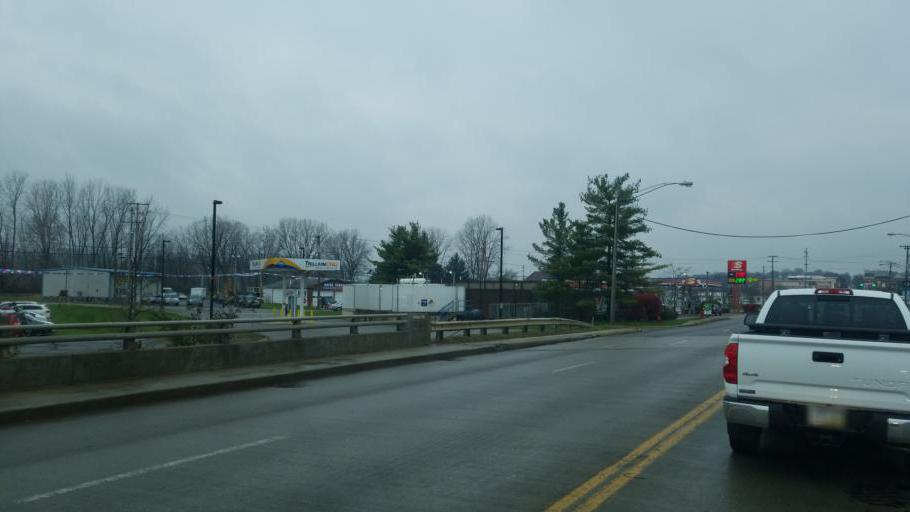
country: US
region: Ohio
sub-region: Knox County
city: Mount Vernon
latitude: 40.3867
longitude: -82.4860
